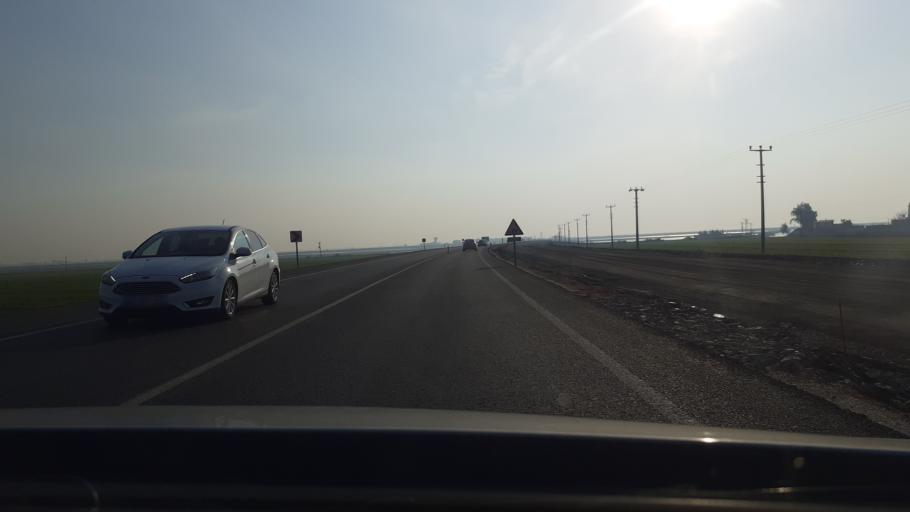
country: TR
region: Hatay
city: Serinyol
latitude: 36.3707
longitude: 36.2521
